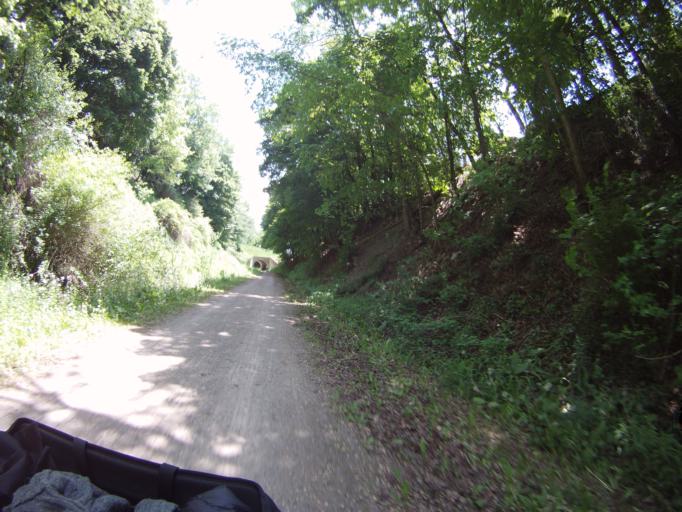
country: US
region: Pennsylvania
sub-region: Somerset County
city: Meyersdale
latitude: 39.8196
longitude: -79.0242
